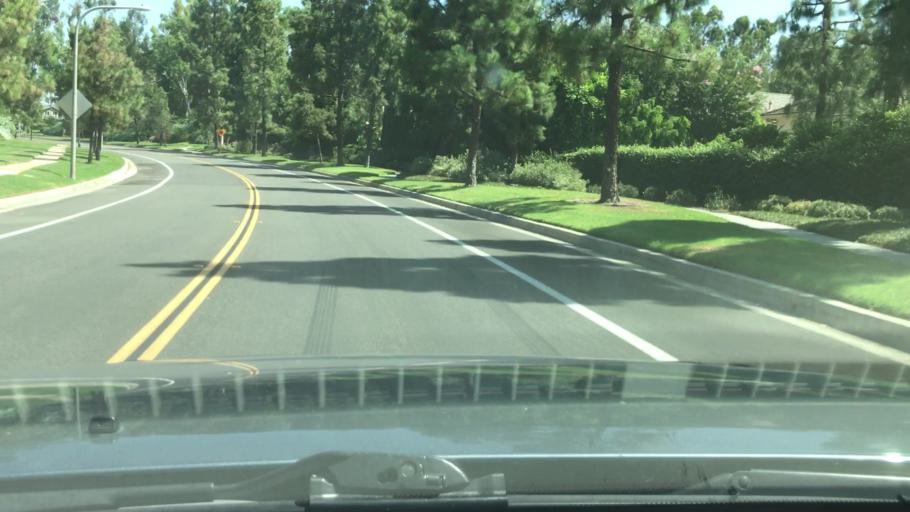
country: US
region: California
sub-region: Orange County
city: Irvine
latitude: 33.6366
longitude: -117.8013
